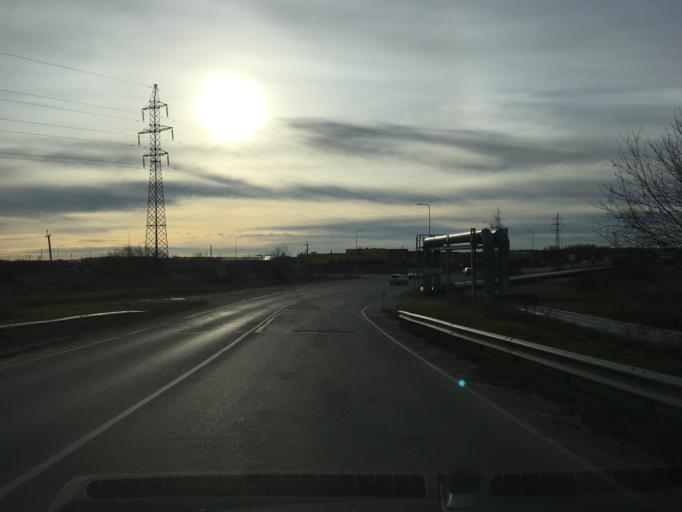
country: EE
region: Ida-Virumaa
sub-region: Narva linn
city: Narva
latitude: 59.3703
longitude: 28.1554
